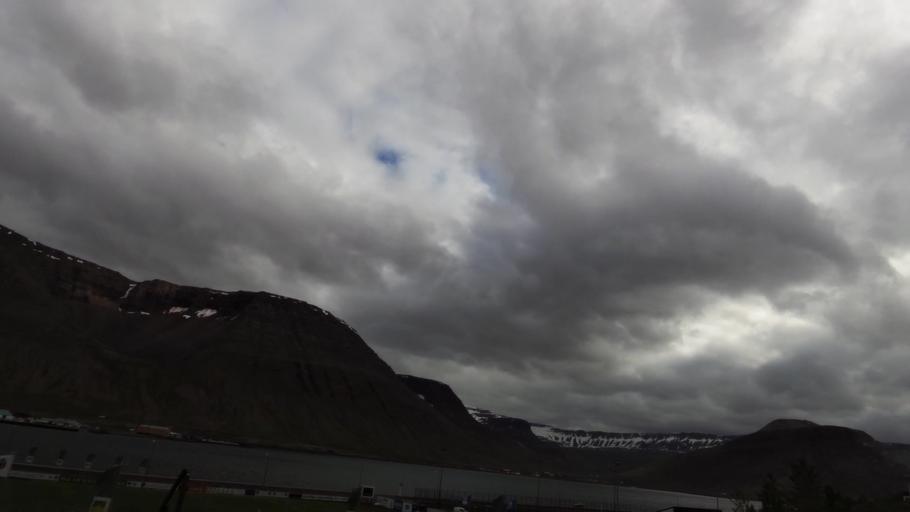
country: IS
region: Westfjords
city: Isafjoerdur
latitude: 66.0736
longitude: -23.1370
